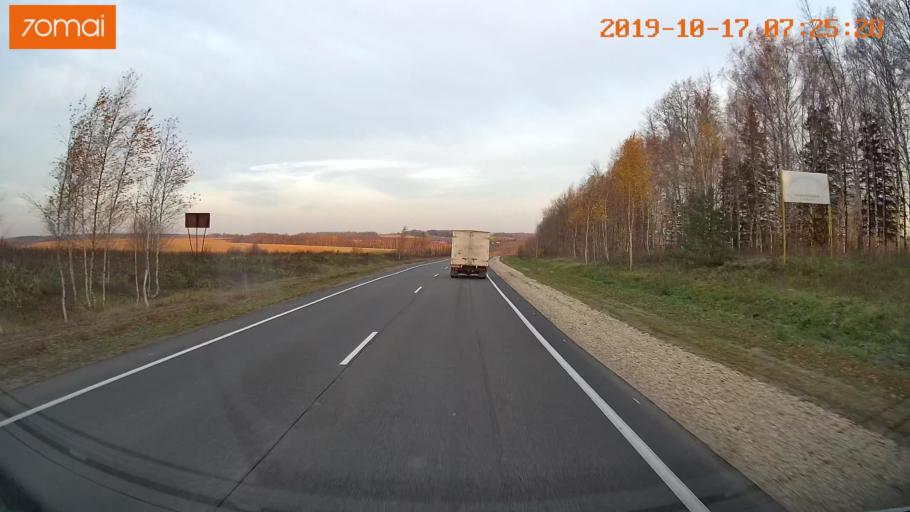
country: RU
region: Ivanovo
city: Gavrilov Posad
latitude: 56.3497
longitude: 40.1034
